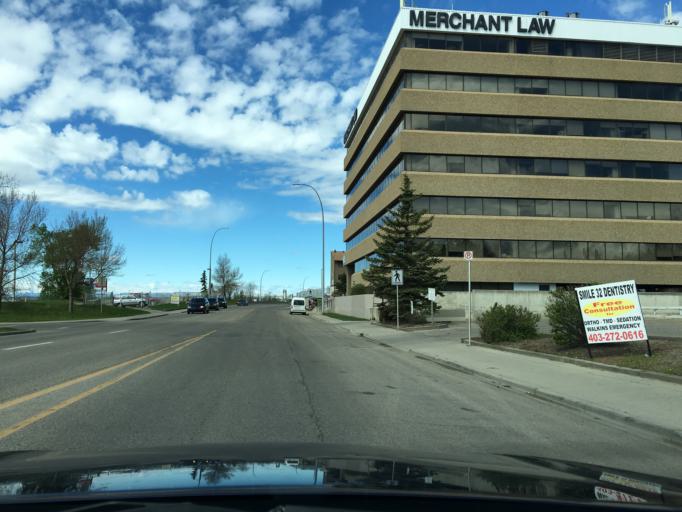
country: CA
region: Alberta
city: Calgary
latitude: 51.0378
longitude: -113.9964
